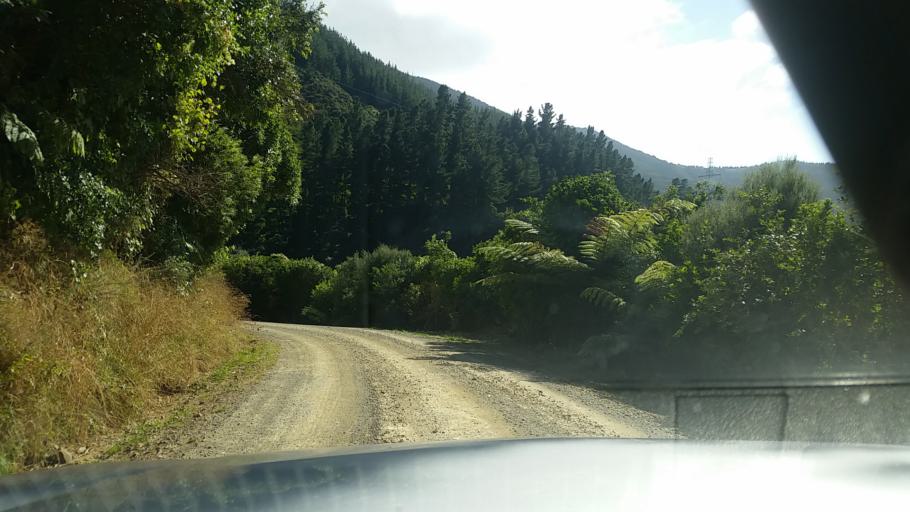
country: NZ
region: Marlborough
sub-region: Marlborough District
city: Picton
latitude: -41.2902
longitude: 174.1711
